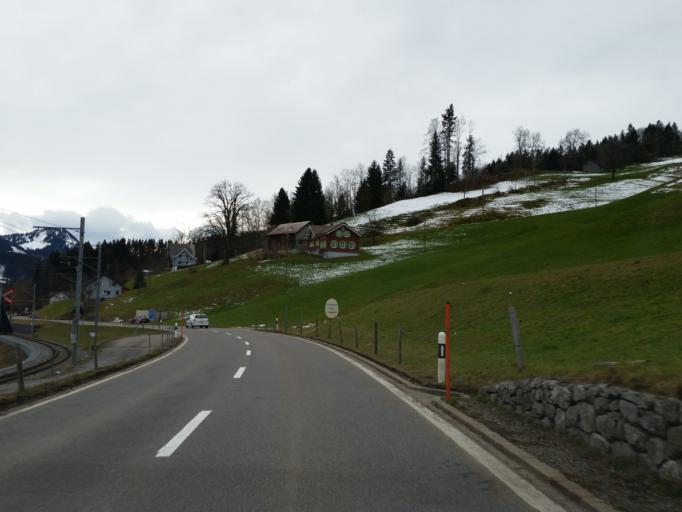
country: CH
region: Appenzell Ausserrhoden
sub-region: Bezirk Hinterland
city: Waldstatt
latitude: 47.3417
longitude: 9.2913
